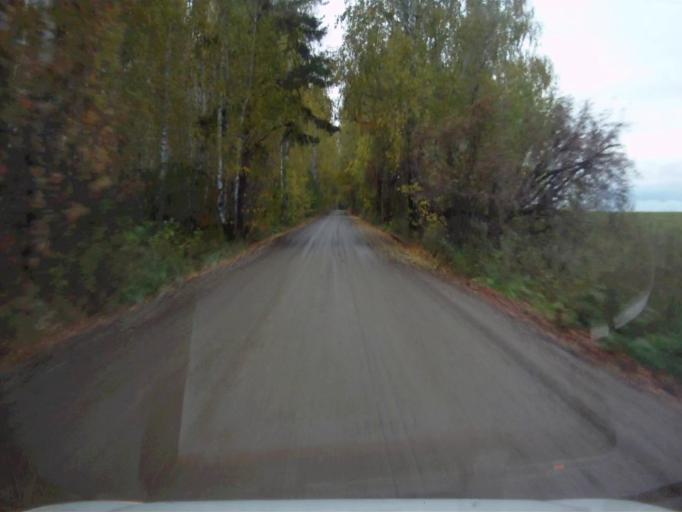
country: RU
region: Sverdlovsk
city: Mikhaylovsk
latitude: 56.1700
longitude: 59.2250
